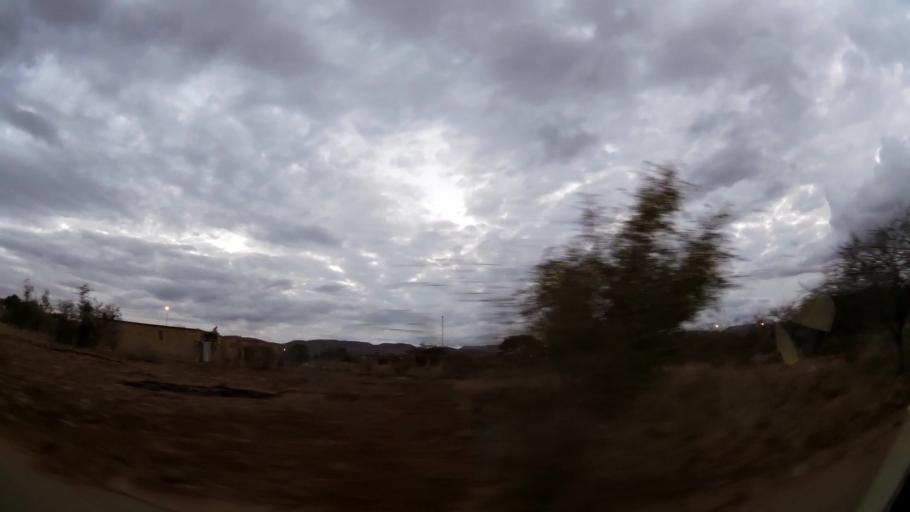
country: ZA
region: Limpopo
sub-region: Waterberg District Municipality
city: Mokopane
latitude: -24.1966
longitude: 28.9985
